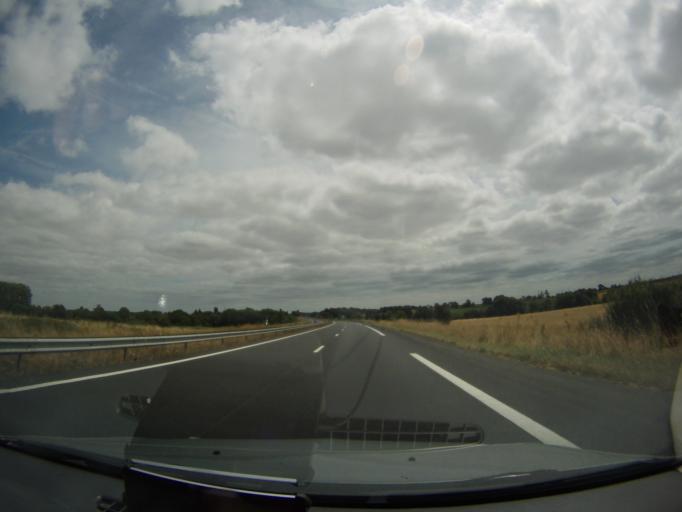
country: FR
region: Pays de la Loire
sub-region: Departement de Maine-et-Loire
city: Saint-Andre-de-la-Marche
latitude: 47.1032
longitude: -1.0266
